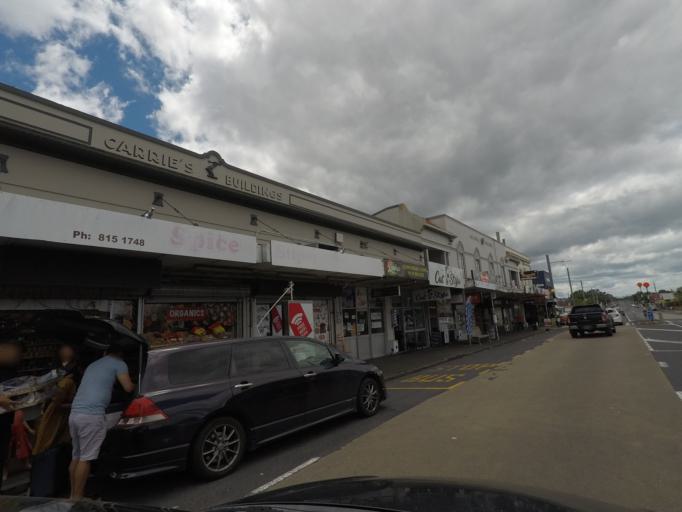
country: NZ
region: Auckland
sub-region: Auckland
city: Auckland
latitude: -36.8919
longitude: 174.7362
